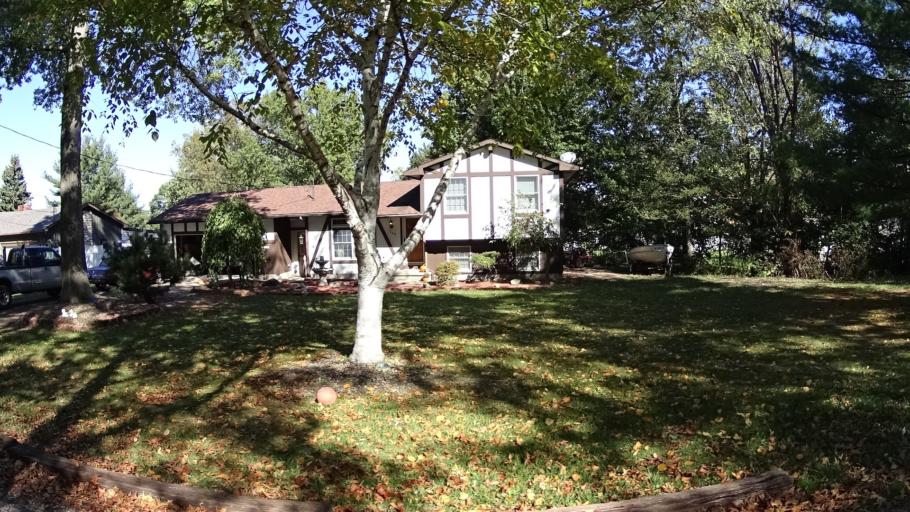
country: US
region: Ohio
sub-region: Lorain County
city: Lorain
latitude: 41.4210
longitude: -82.1570
